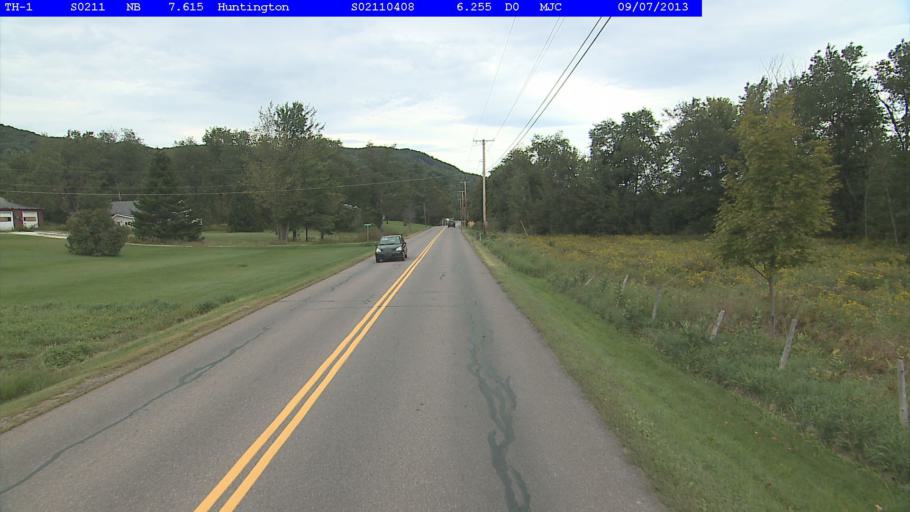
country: US
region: Vermont
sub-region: Chittenden County
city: Hinesburg
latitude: 44.3095
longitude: -72.9857
